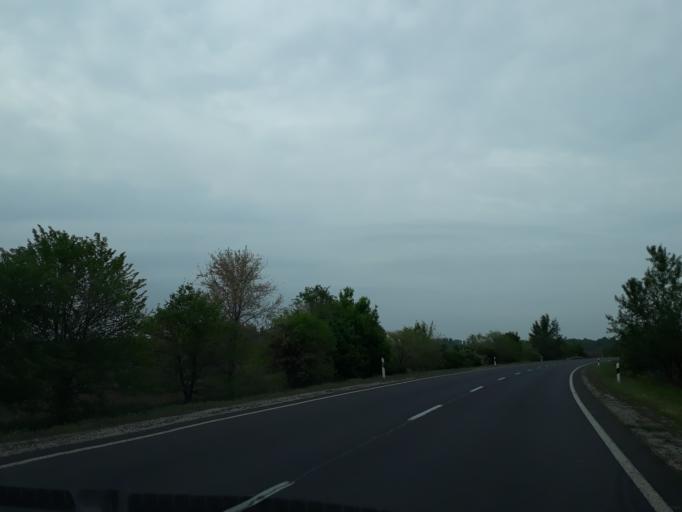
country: HU
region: Szabolcs-Szatmar-Bereg
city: Nyirtass
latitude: 48.0871
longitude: 21.9867
